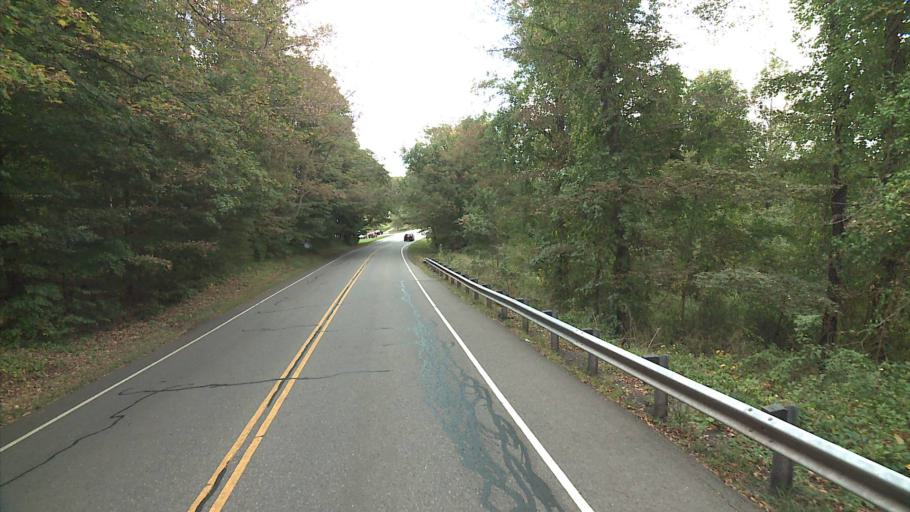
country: US
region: Connecticut
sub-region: Middlesex County
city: Durham
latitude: 41.4968
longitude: -72.7188
